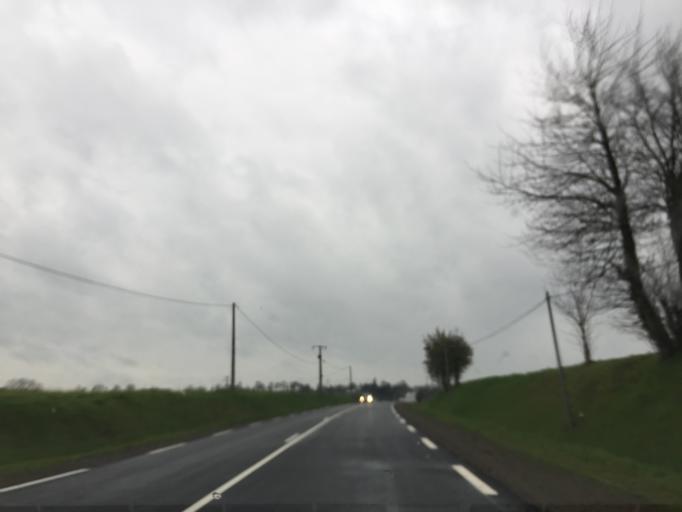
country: FR
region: Brittany
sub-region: Departement d'Ille-et-Vilaine
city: Luitre
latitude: 48.2934
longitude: -1.1583
